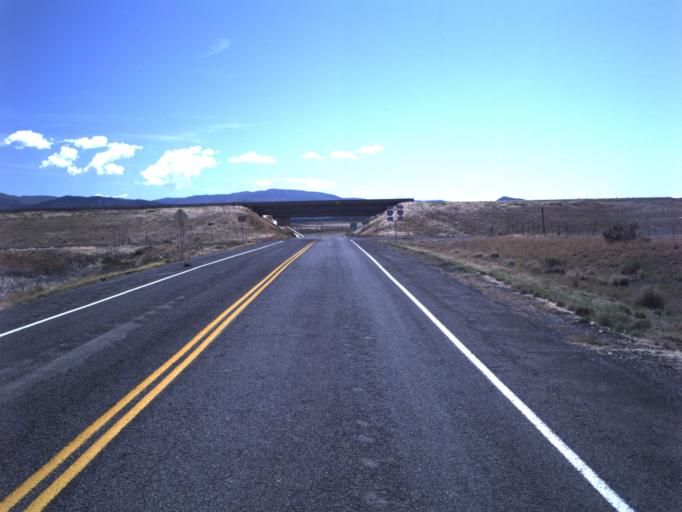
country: US
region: Utah
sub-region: Juab County
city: Nephi
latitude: 39.4846
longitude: -111.9806
